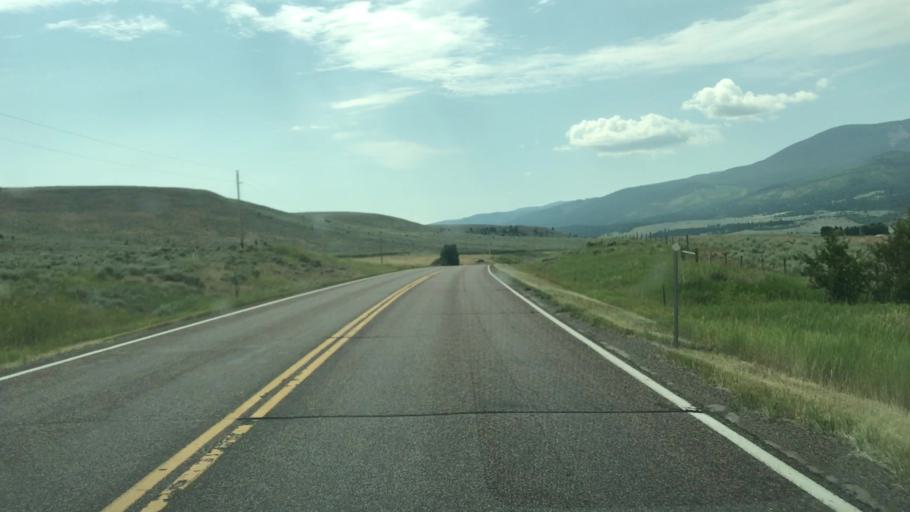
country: US
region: Montana
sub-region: Lewis and Clark County
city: Lincoln
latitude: 46.8549
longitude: -112.9064
